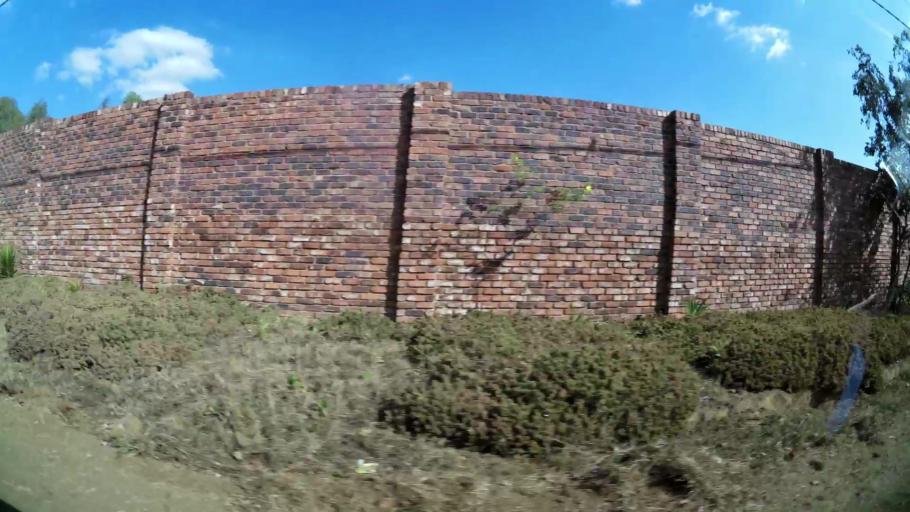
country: ZA
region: Gauteng
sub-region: Ekurhuleni Metropolitan Municipality
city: Benoni
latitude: -26.0796
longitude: 28.3541
